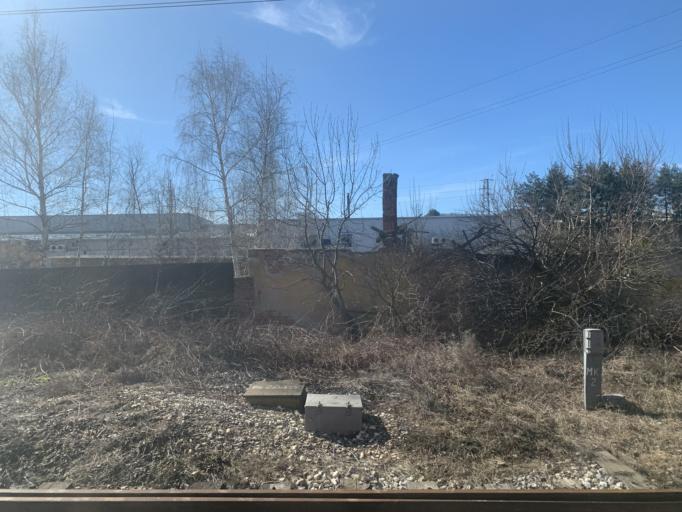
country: BG
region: Sofiya
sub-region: Obshtina Gorna Malina
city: Gorna Malina
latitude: 42.5580
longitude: 23.7029
